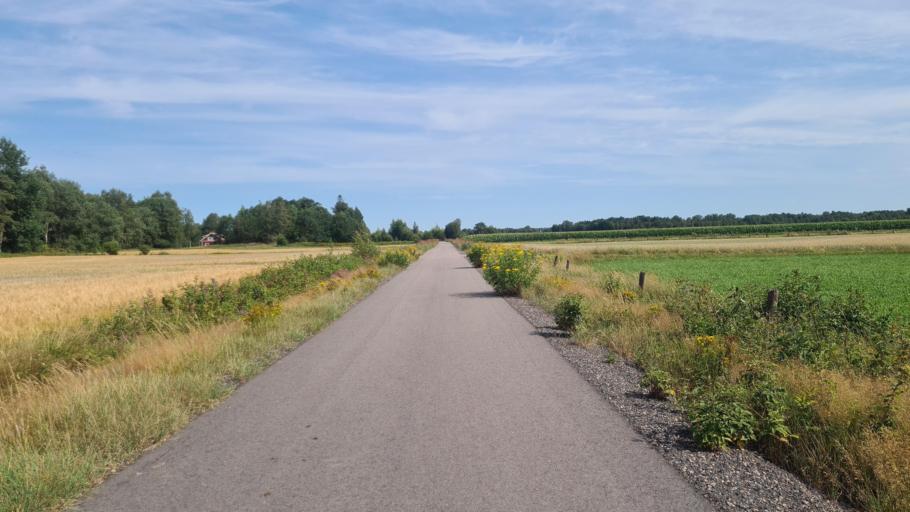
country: SE
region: Kronoberg
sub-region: Ljungby Kommun
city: Lagan
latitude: 56.8956
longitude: 13.9863
